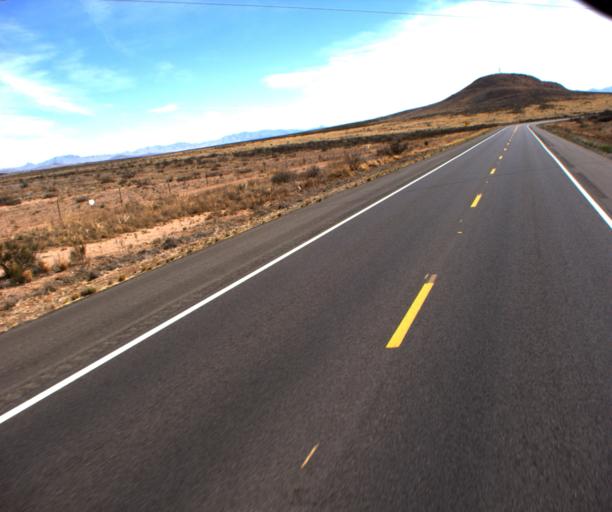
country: US
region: Arizona
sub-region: Cochise County
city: Willcox
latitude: 31.9055
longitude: -109.7248
